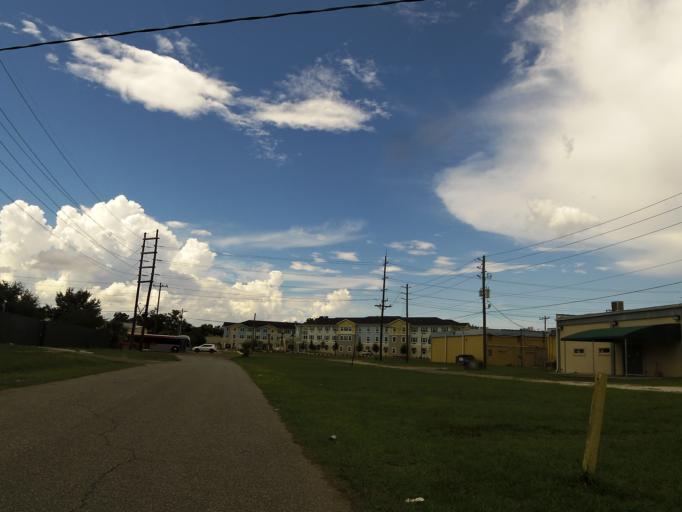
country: US
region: Florida
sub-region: Duval County
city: Jacksonville
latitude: 30.3717
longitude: -81.6585
